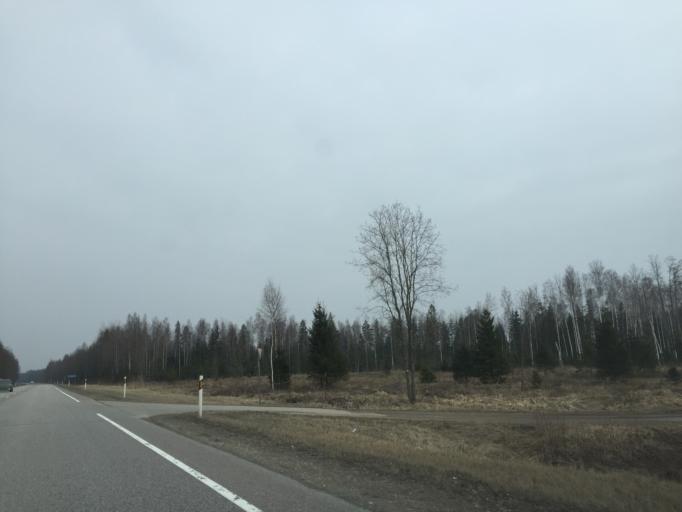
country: LV
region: Salacgrivas
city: Ainazi
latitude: 58.0505
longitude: 24.5105
